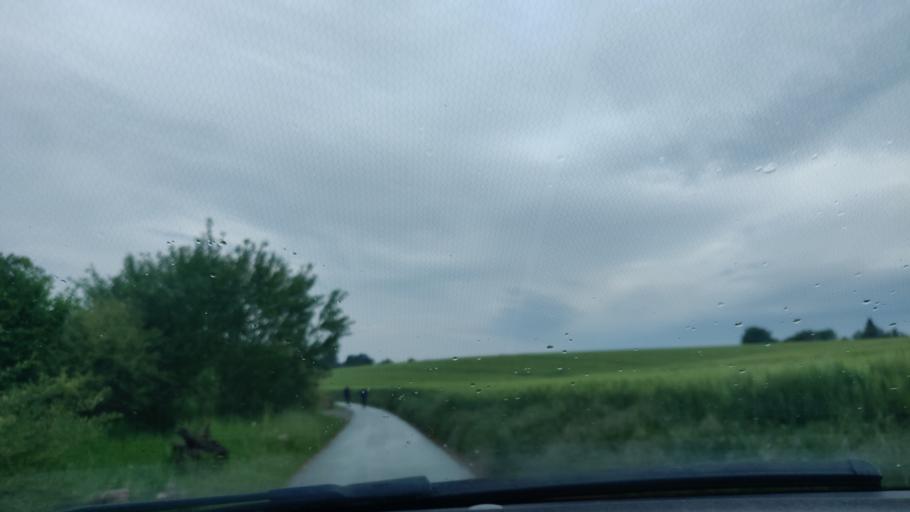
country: DE
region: North Rhine-Westphalia
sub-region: Regierungsbezirk Dusseldorf
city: Heiligenhaus
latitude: 51.3026
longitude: 6.9247
